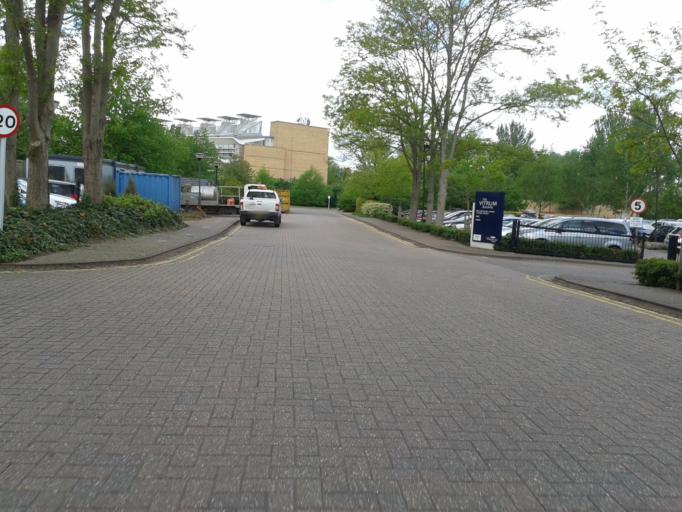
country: GB
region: England
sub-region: Cambridgeshire
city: Waterbeach
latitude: 52.2356
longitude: 0.1548
